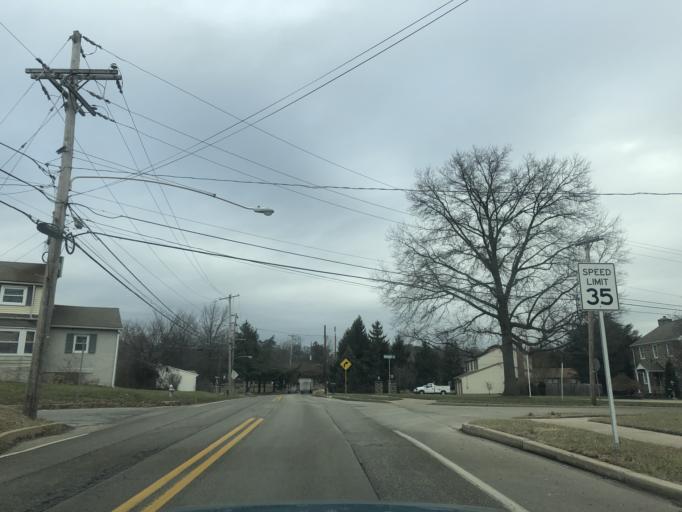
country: US
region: Pennsylvania
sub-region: Montgomery County
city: Conshohocken
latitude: 40.1086
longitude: -75.3108
